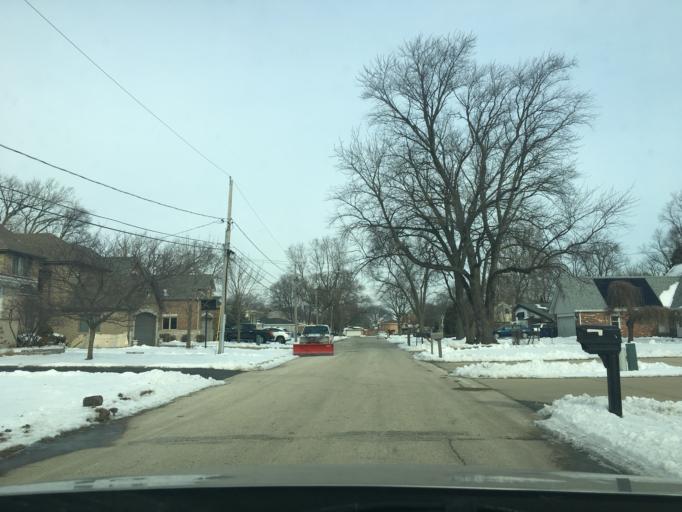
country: US
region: Illinois
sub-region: Cook County
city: Rosemont
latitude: 42.0111
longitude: -87.9016
